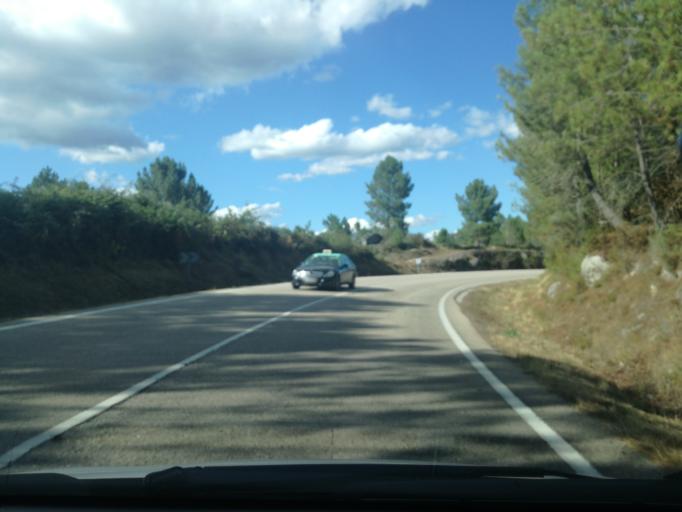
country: ES
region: Galicia
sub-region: Provincia de Ourense
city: Lobios
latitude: 41.8868
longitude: -8.0959
